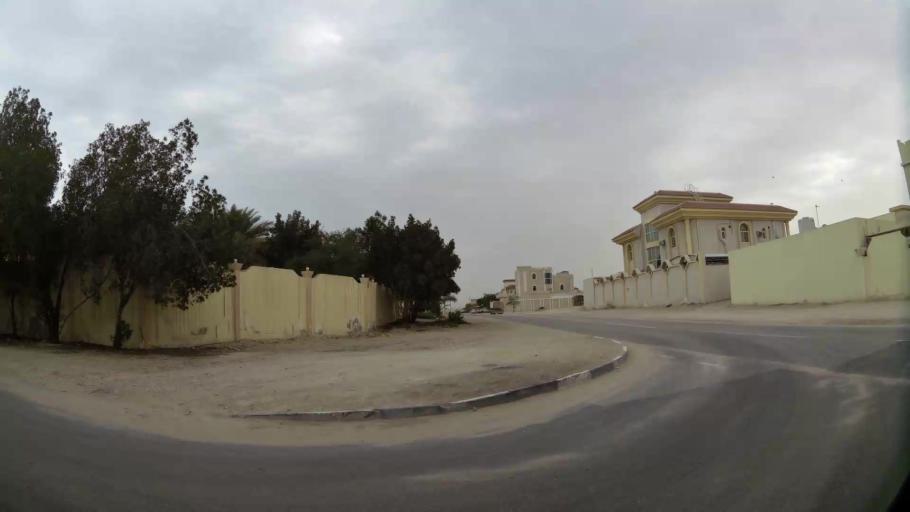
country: QA
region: Baladiyat ar Rayyan
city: Ar Rayyan
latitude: 25.3446
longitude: 51.4630
